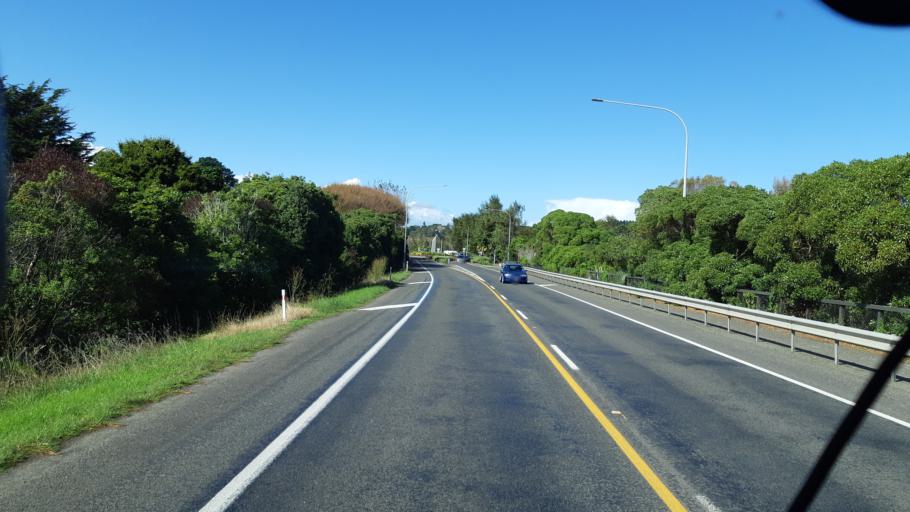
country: NZ
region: Manawatu-Wanganui
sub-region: Wanganui District
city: Wanganui
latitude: -39.9472
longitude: 175.0490
